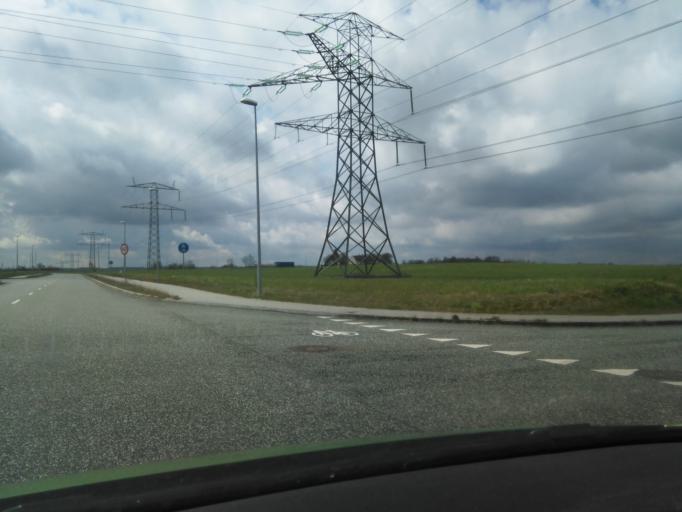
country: DK
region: Central Jutland
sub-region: Arhus Kommune
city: Framlev
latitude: 56.1559
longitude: 10.0590
